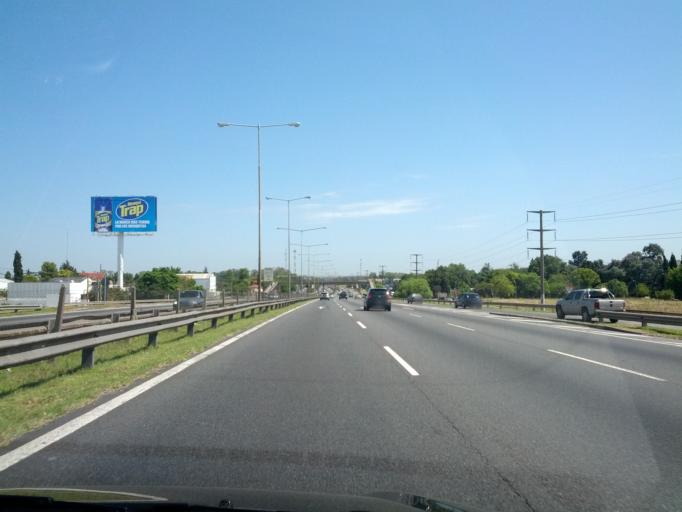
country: AR
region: Buenos Aires
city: Santa Catalina - Dique Lujan
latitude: -34.4070
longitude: -58.7310
